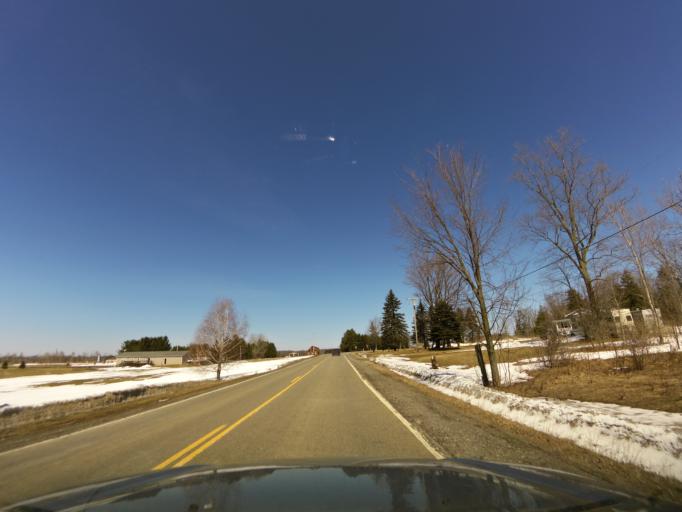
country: US
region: New York
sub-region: Cattaraugus County
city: Yorkshire
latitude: 42.5499
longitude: -78.4562
